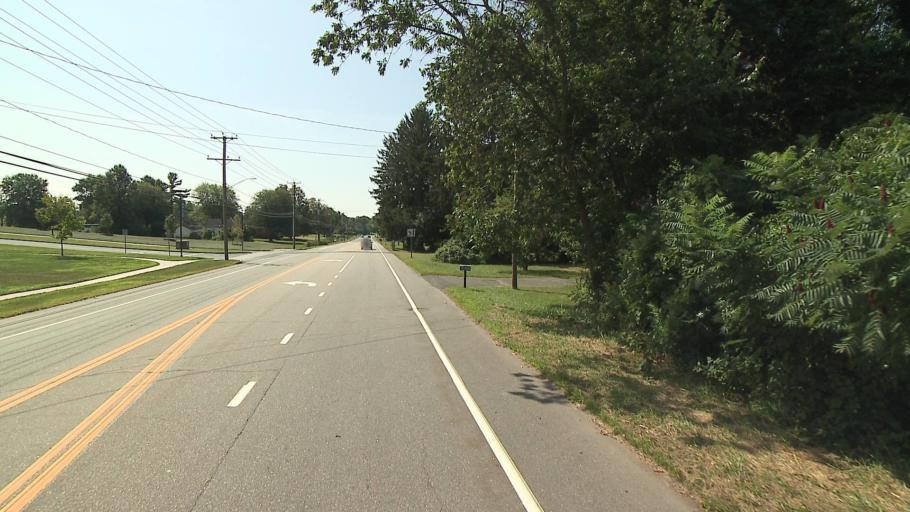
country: US
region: Connecticut
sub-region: Hartford County
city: Enfield
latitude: 41.9489
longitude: -72.6021
